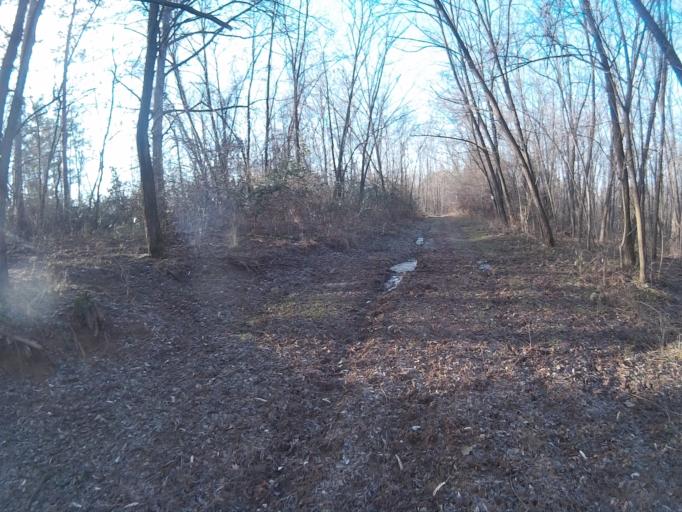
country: HU
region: Nograd
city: Bercel
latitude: 47.9520
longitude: 19.4434
